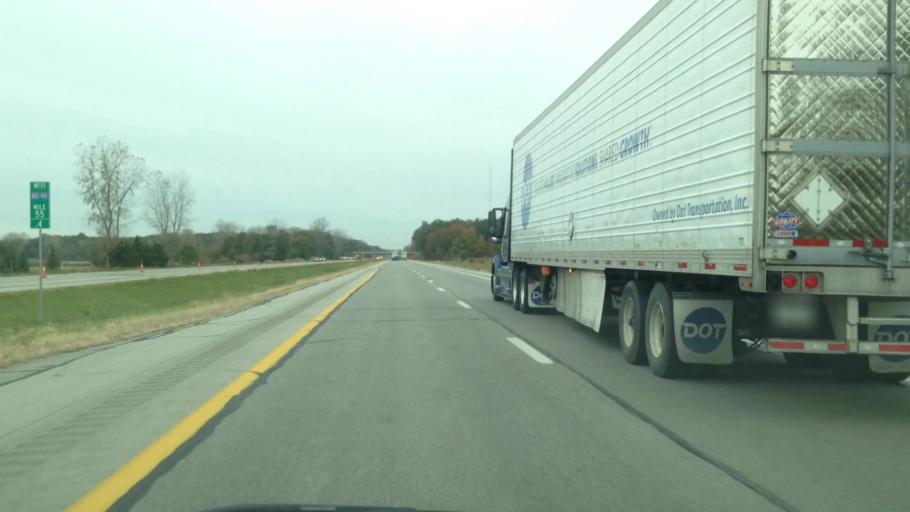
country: US
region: Ohio
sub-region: Lucas County
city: Holland
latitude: 41.5917
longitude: -83.7501
